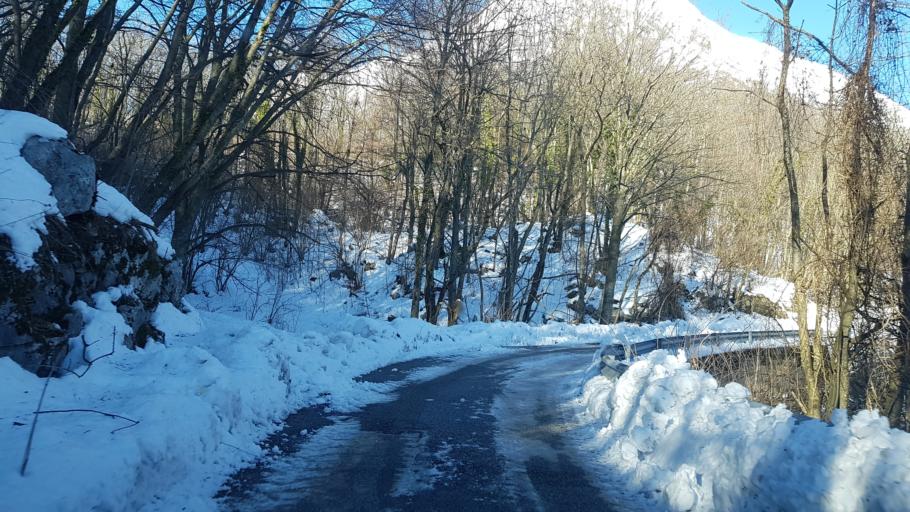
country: IT
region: Friuli Venezia Giulia
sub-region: Provincia di Udine
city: Forgaria nel Friuli
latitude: 46.2635
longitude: 12.9957
